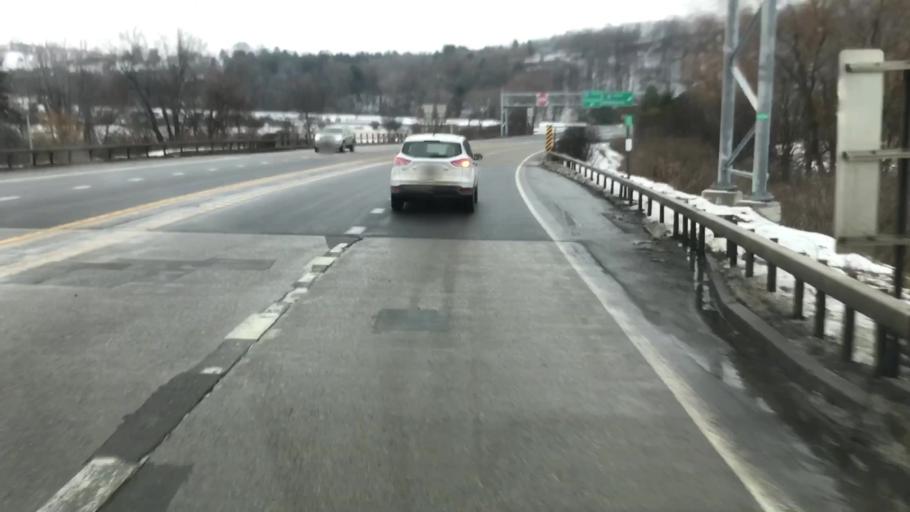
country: US
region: New York
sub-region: Cortland County
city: Homer
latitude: 42.6277
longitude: -76.1810
